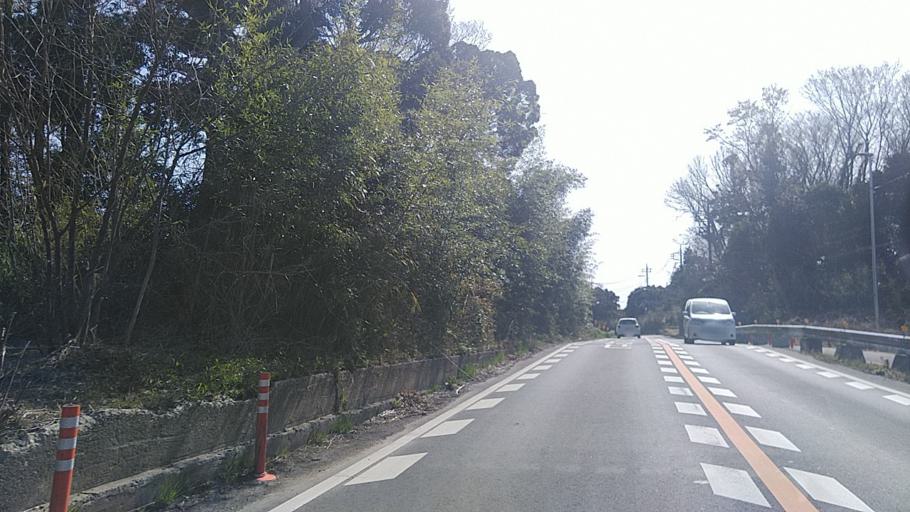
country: JP
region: Ibaraki
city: Fujishiro
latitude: 35.8818
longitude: 140.1209
